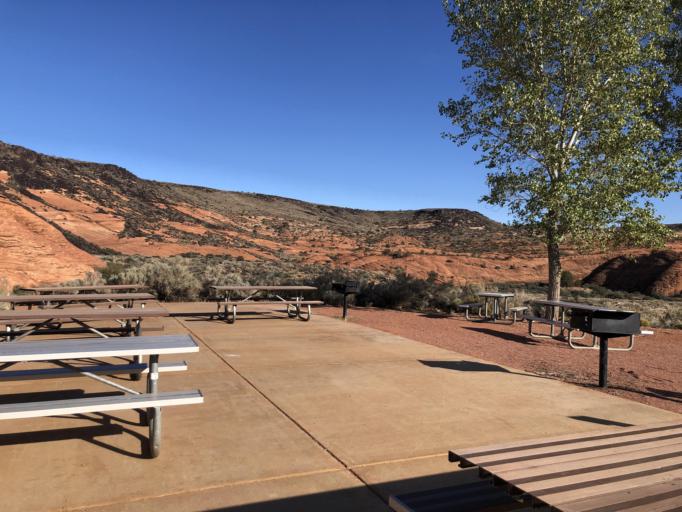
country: US
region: Utah
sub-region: Washington County
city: Ivins
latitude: 37.2109
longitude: -113.6420
